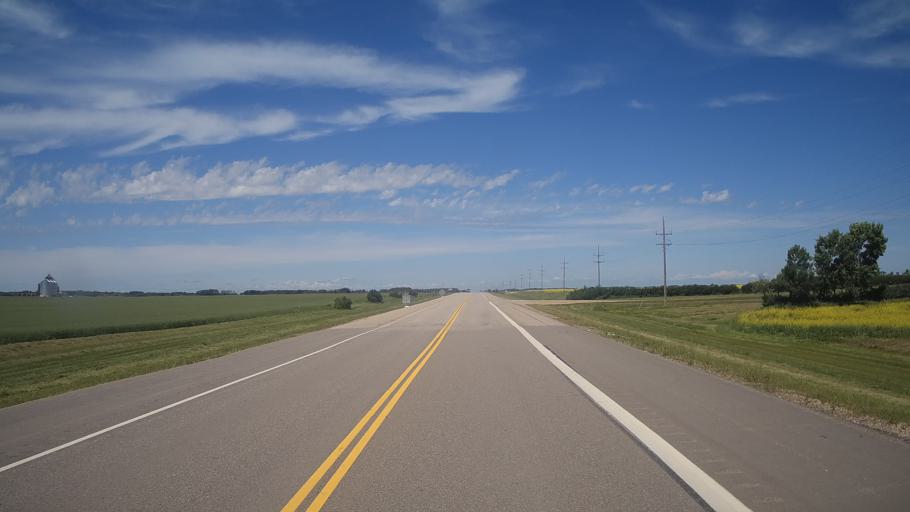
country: CA
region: Saskatchewan
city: Langenburg
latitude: 50.6318
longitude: -101.2763
